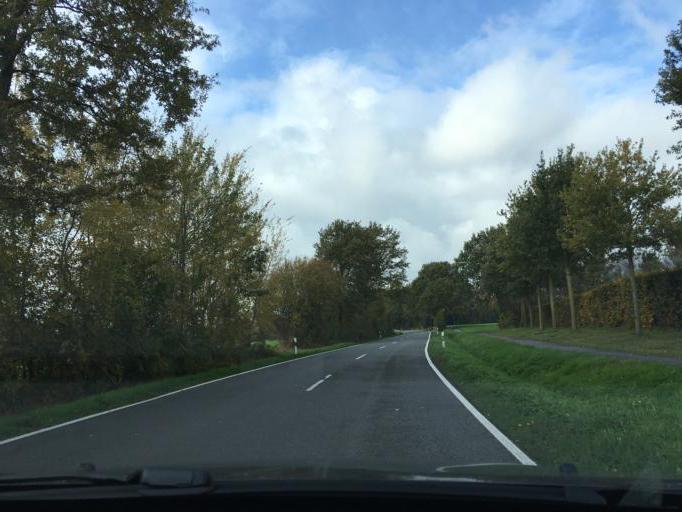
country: DE
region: North Rhine-Westphalia
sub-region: Regierungsbezirk Munster
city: Vreden
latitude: 52.0530
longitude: 6.7733
